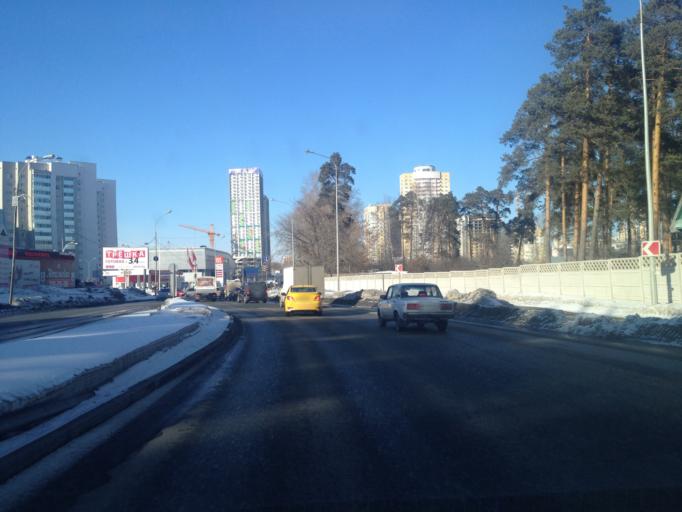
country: RU
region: Sverdlovsk
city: Sovkhoznyy
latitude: 56.7955
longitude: 60.5963
